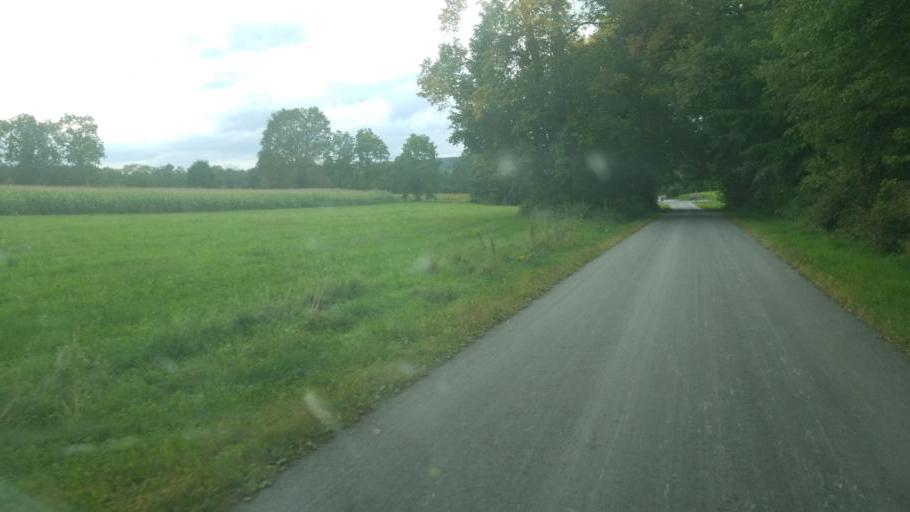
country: US
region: Pennsylvania
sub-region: Mercer County
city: Greenville
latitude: 41.4775
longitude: -80.3447
